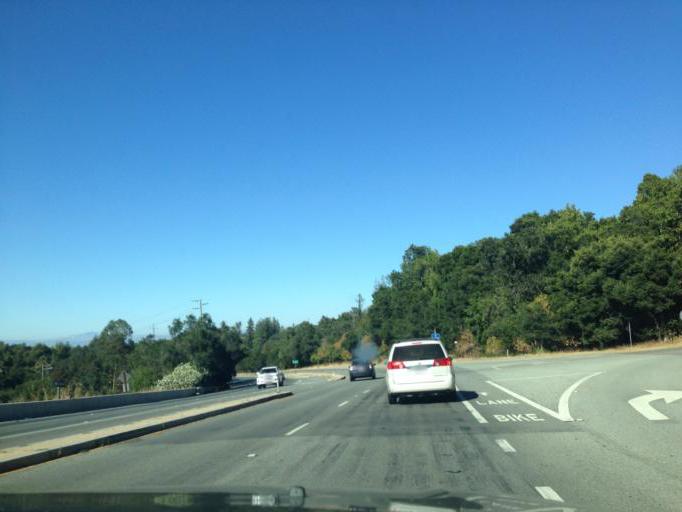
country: US
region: California
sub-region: San Mateo County
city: Woodside
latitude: 37.4404
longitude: -122.2377
